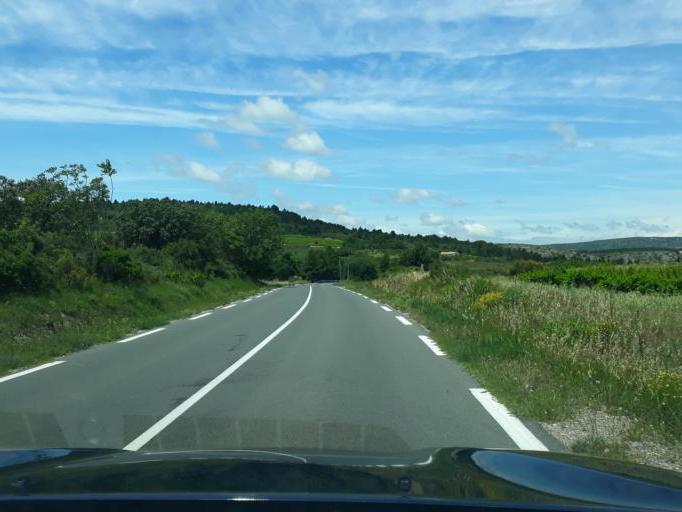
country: FR
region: Languedoc-Roussillon
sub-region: Departement de l'Aude
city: Portel-des-Corbieres
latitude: 43.0423
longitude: 2.9350
